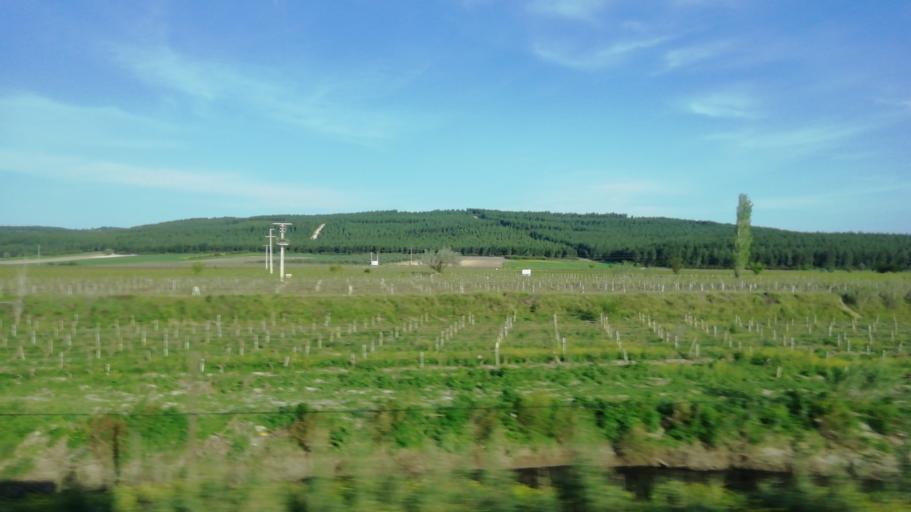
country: TR
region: Manisa
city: Halitpasa
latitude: 38.8030
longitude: 27.6905
